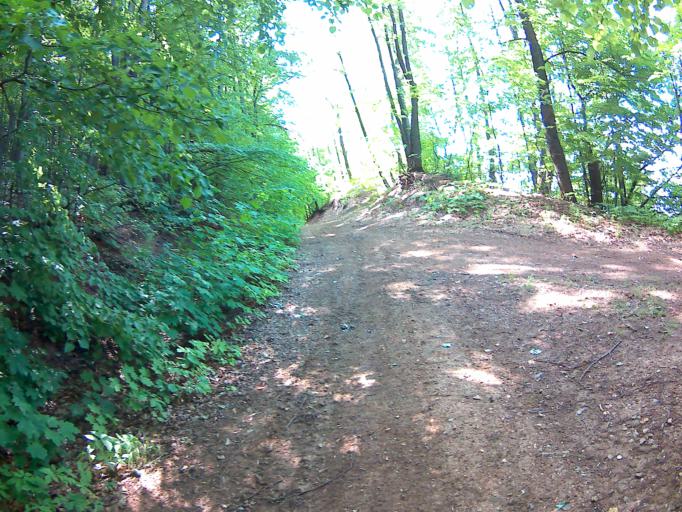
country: RU
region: Nizjnij Novgorod
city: Nizhniy Novgorod
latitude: 56.2400
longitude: 43.9395
